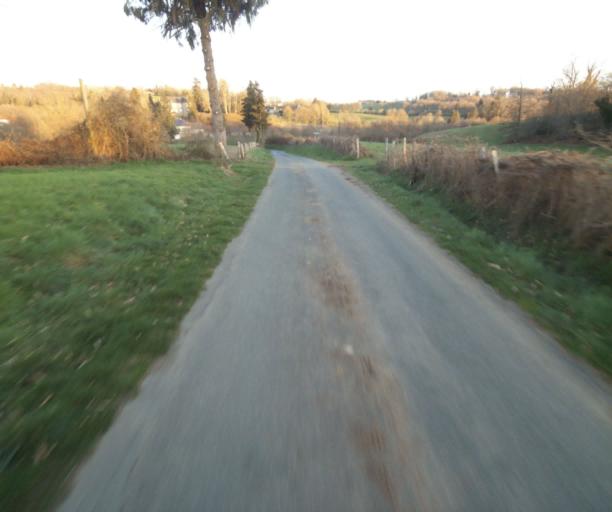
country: FR
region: Limousin
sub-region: Departement de la Correze
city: Uzerche
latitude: 45.3684
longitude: 1.6148
